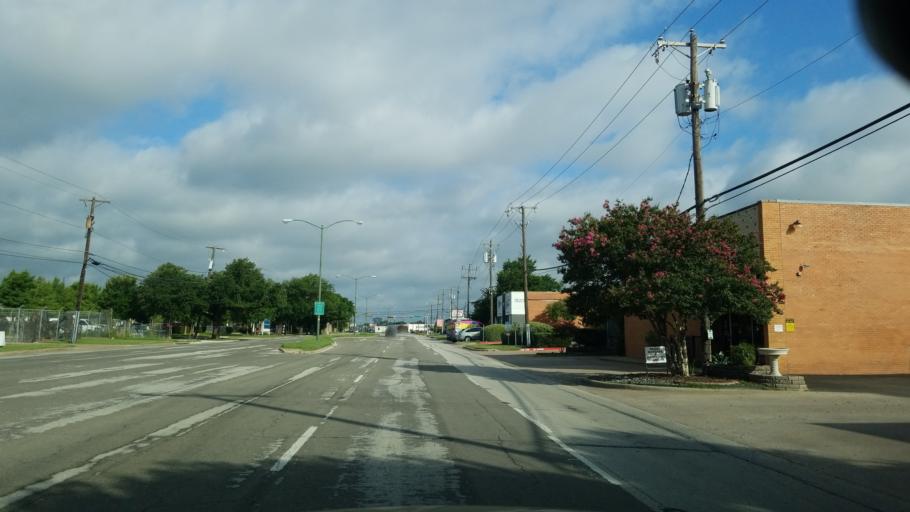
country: US
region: Texas
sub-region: Dallas County
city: Dallas
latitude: 32.7931
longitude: -96.8244
